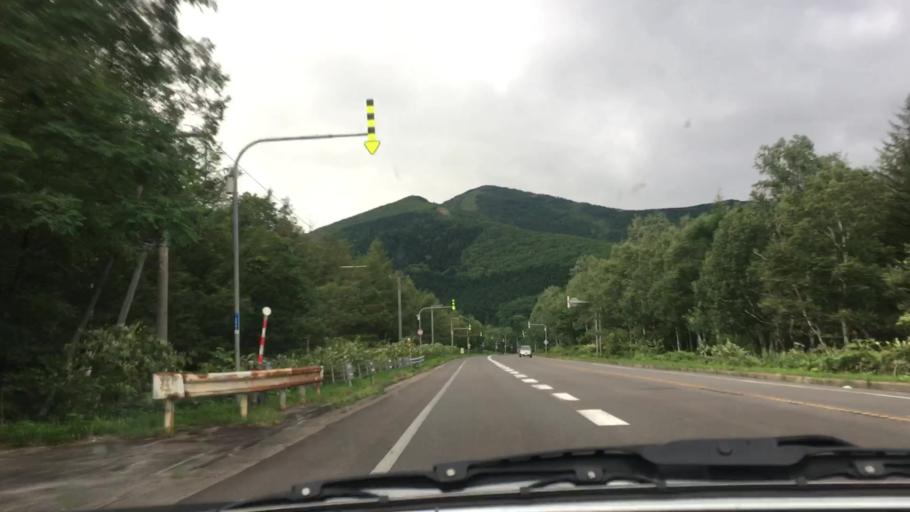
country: JP
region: Hokkaido
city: Otofuke
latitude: 43.1620
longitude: 142.8135
